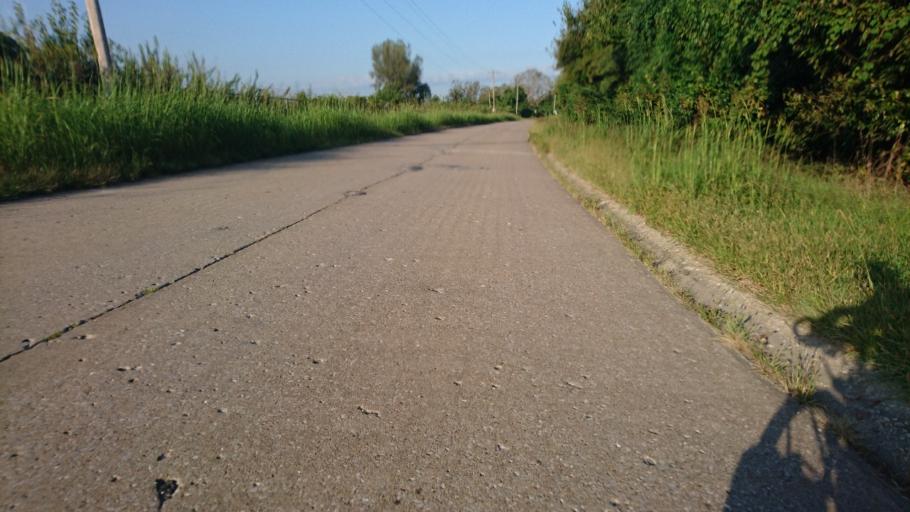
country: US
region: Missouri
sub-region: Saint Louis County
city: Glasgow Village
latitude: 38.7568
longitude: -90.1578
